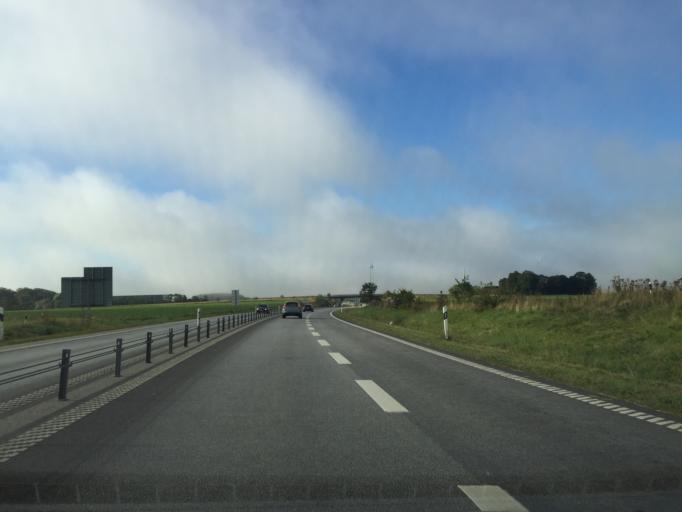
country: SE
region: Skane
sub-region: Staffanstorps Kommun
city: Hjaerup
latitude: 55.7079
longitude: 13.1464
